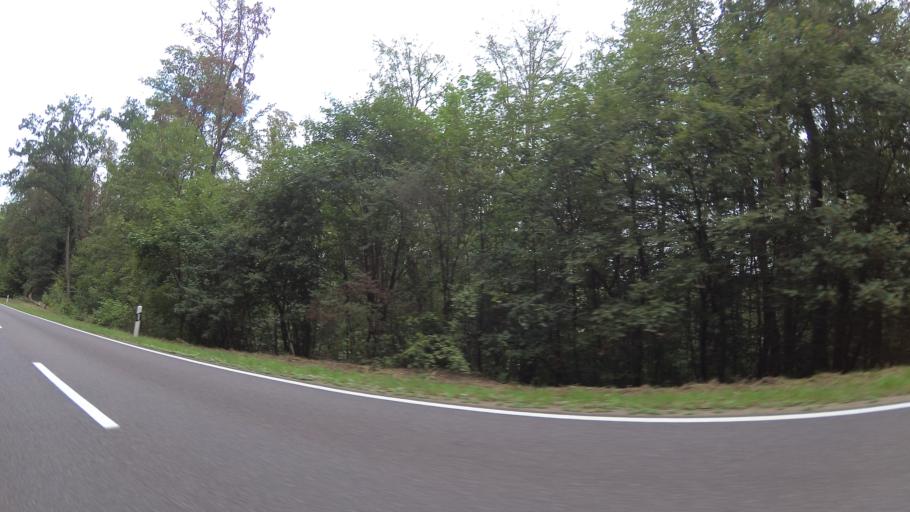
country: FR
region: Lorraine
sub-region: Departement de la Moselle
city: Sarreguemines
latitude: 49.1405
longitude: 7.0803
